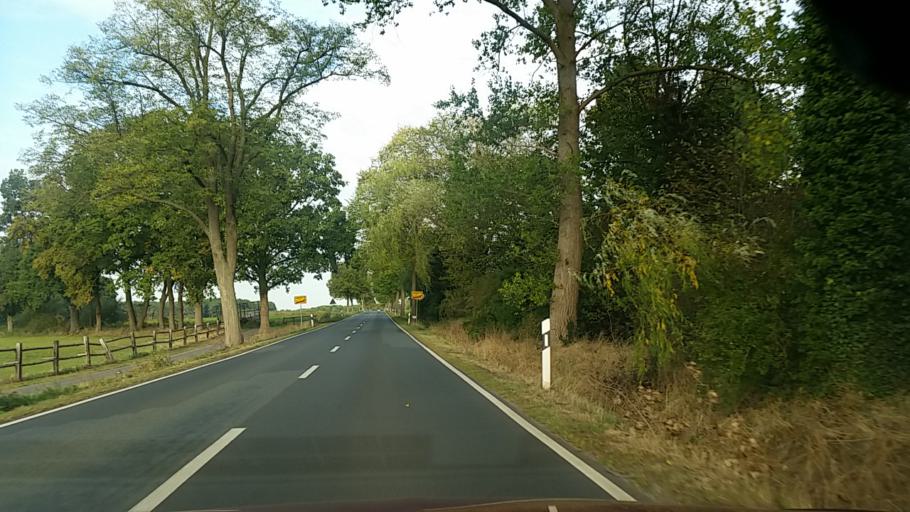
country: DE
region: Lower Saxony
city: Ahnsbeck
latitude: 52.6130
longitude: 10.2785
